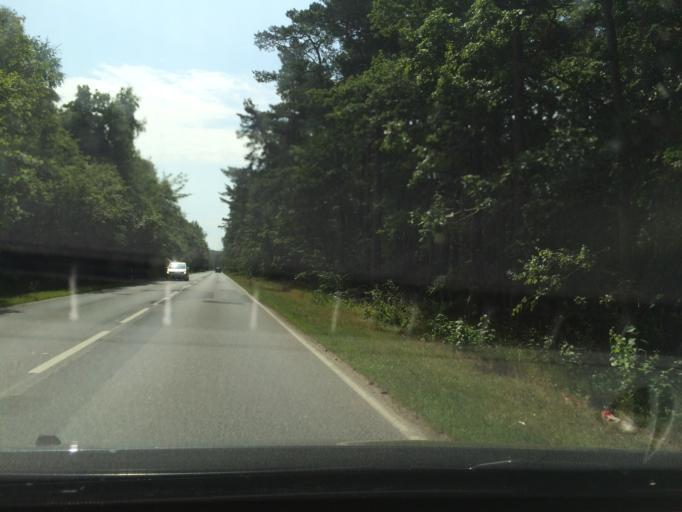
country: DE
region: Mecklenburg-Vorpommern
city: Ostseebad Binz
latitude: 54.4345
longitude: 13.5709
